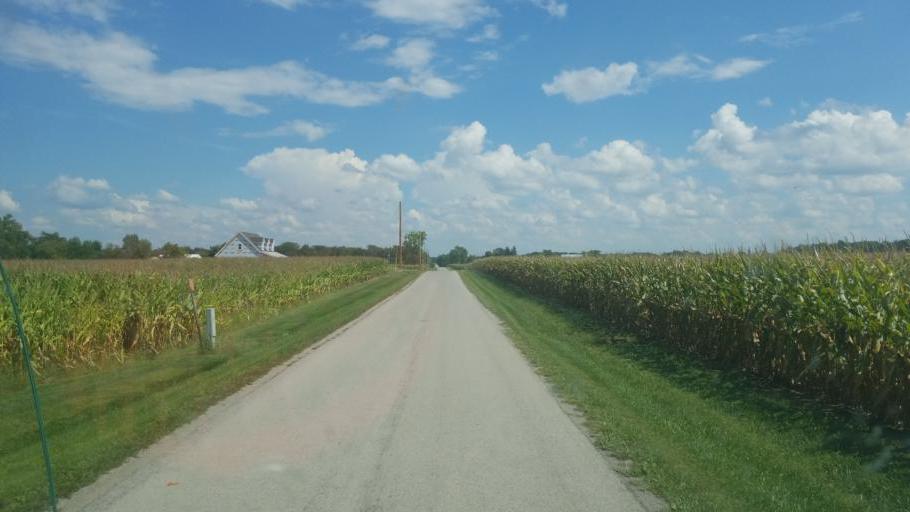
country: US
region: Ohio
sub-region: Wyandot County
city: Carey
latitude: 40.8755
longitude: -83.3959
